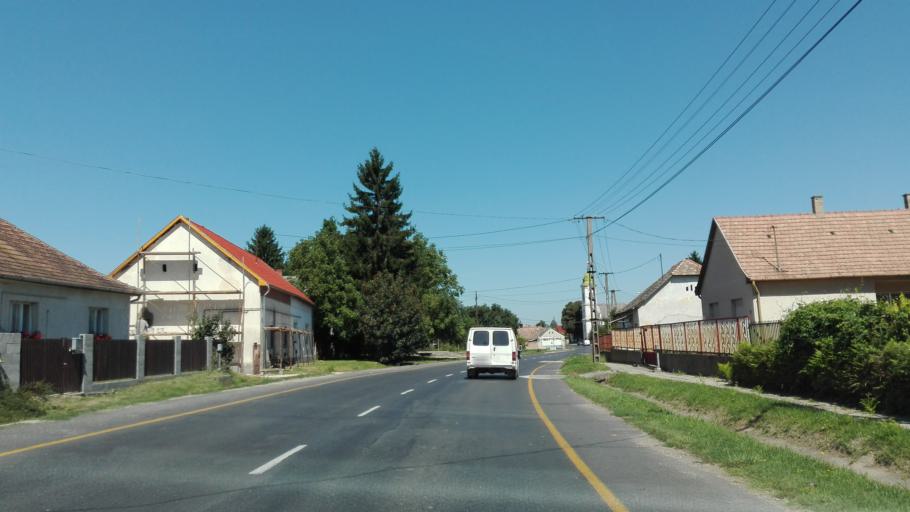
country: HU
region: Fejer
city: Mezoszilas
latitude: 46.8080
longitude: 18.4848
